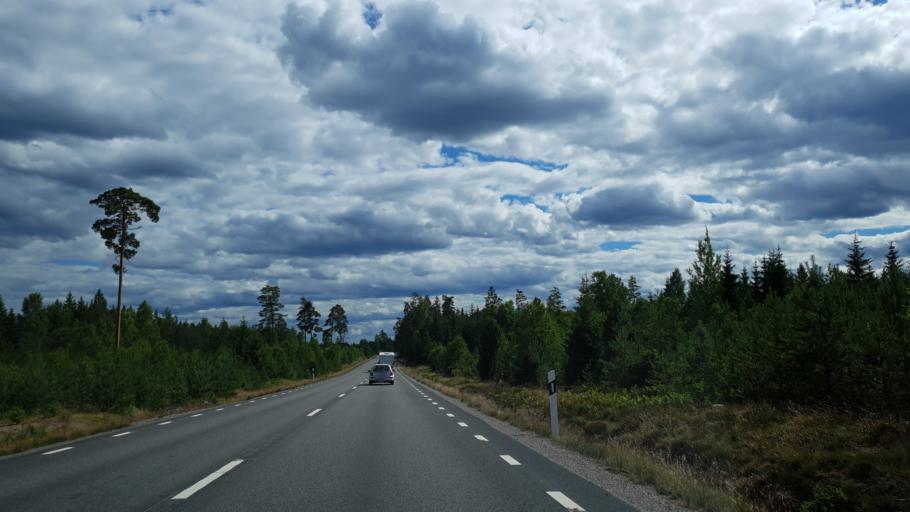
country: SE
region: Kronoberg
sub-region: Lessebo Kommun
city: Lessebo
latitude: 56.8092
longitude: 15.4119
